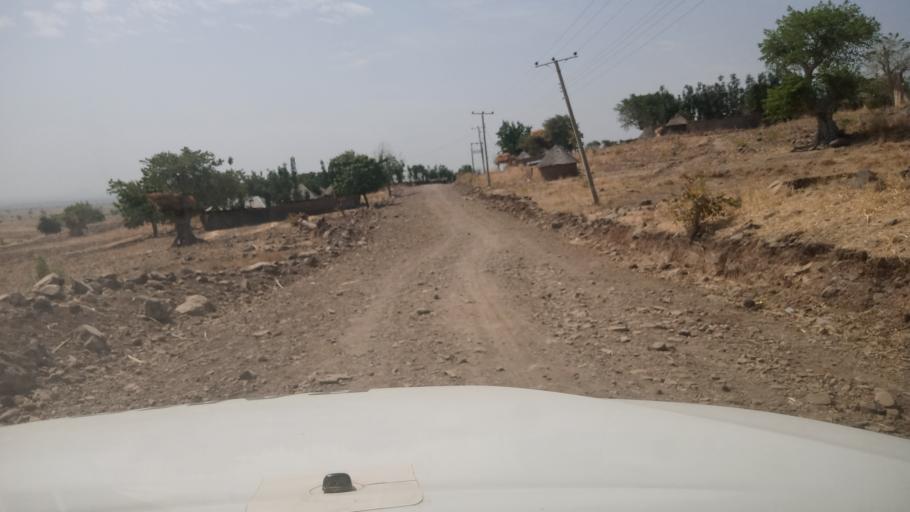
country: NG
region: Adamawa
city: Numan
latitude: 9.6964
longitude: 11.9192
